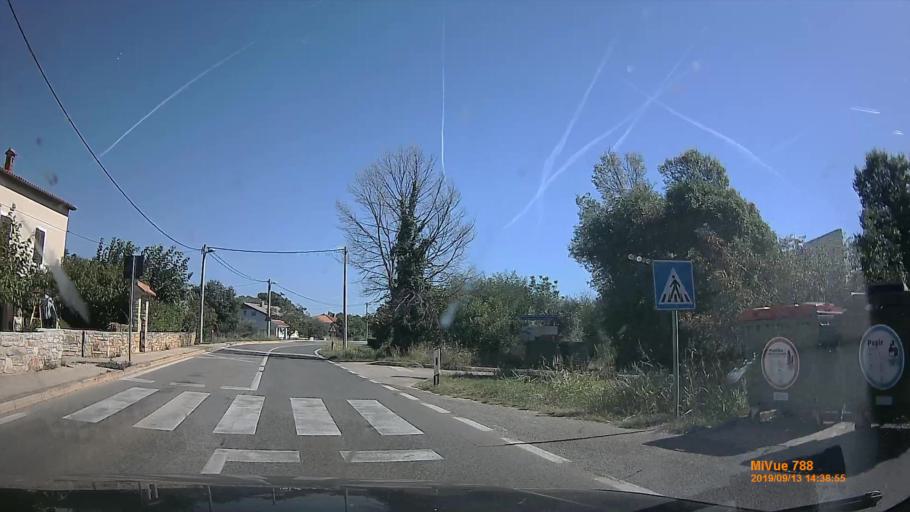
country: HR
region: Istarska
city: Umag
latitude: 45.3984
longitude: 13.5397
